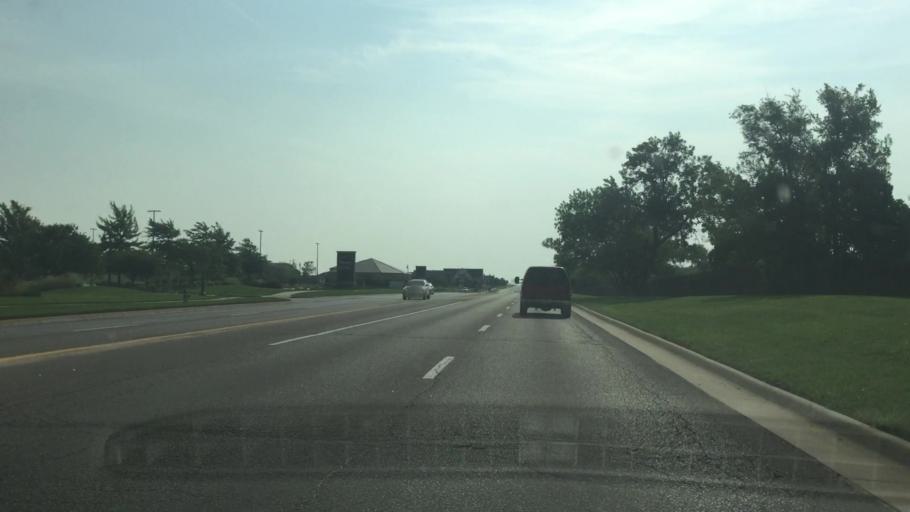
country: US
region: Kansas
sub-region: Sedgwick County
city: Bellaire
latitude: 37.7084
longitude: -97.2212
